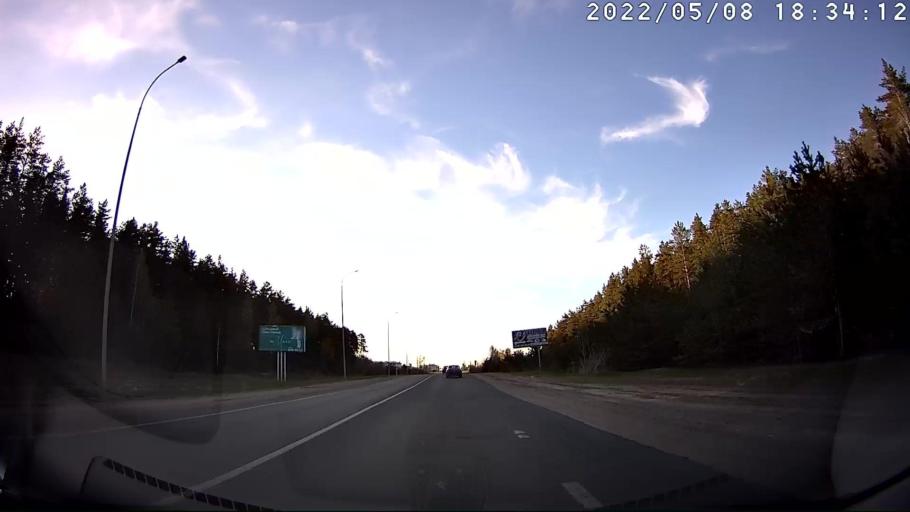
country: RU
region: Mariy-El
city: Volzhsk
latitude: 55.8980
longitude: 48.3563
